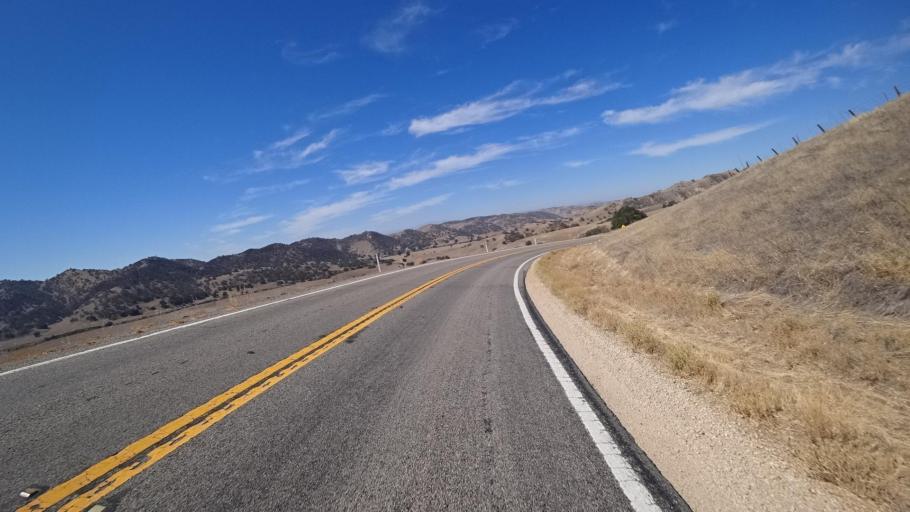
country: US
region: California
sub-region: Monterey County
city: King City
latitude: 36.1896
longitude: -120.8029
